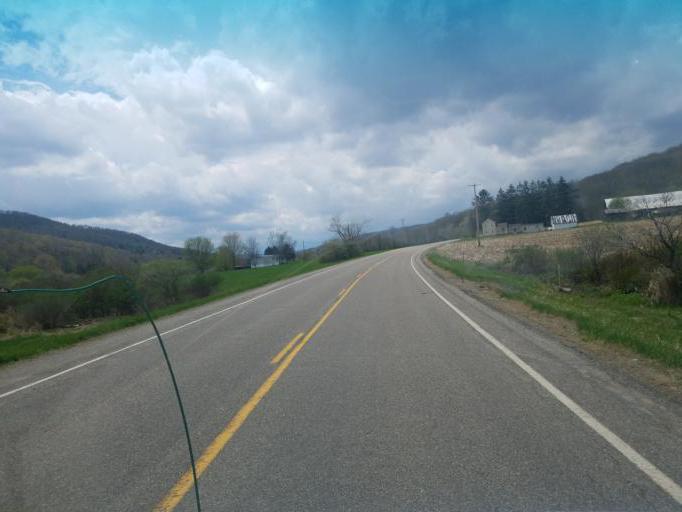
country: US
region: New York
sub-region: Allegany County
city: Andover
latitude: 42.0294
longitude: -77.7966
